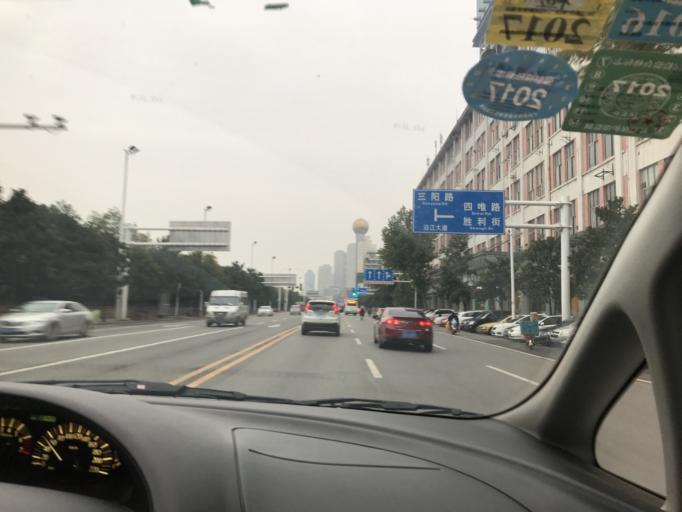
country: CN
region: Hubei
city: Jiang'an
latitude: 30.6019
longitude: 114.3041
